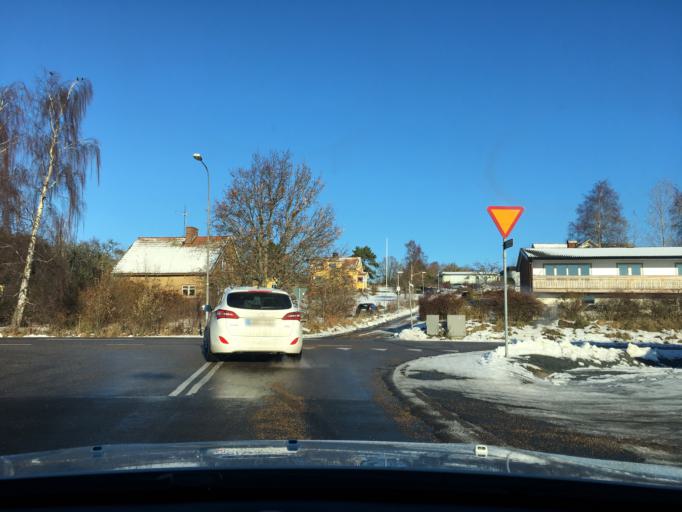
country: SE
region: Vaestra Goetaland
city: Svanesund
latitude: 58.1427
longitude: 11.8219
